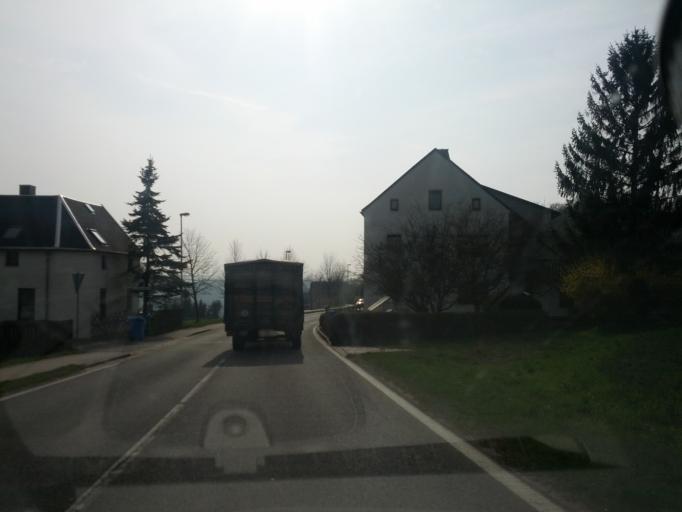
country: DE
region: Saxony
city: Kirchberg
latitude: 50.6297
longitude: 12.5545
